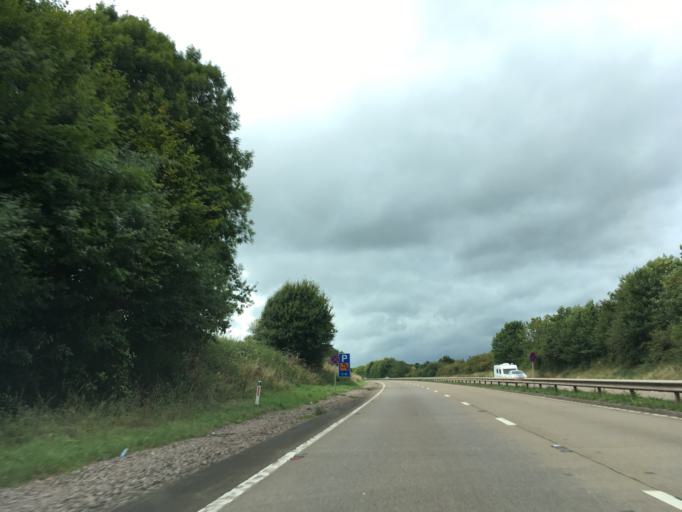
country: GB
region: Wales
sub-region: Monmouthshire
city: Llanarth
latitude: 51.7735
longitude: -2.8742
